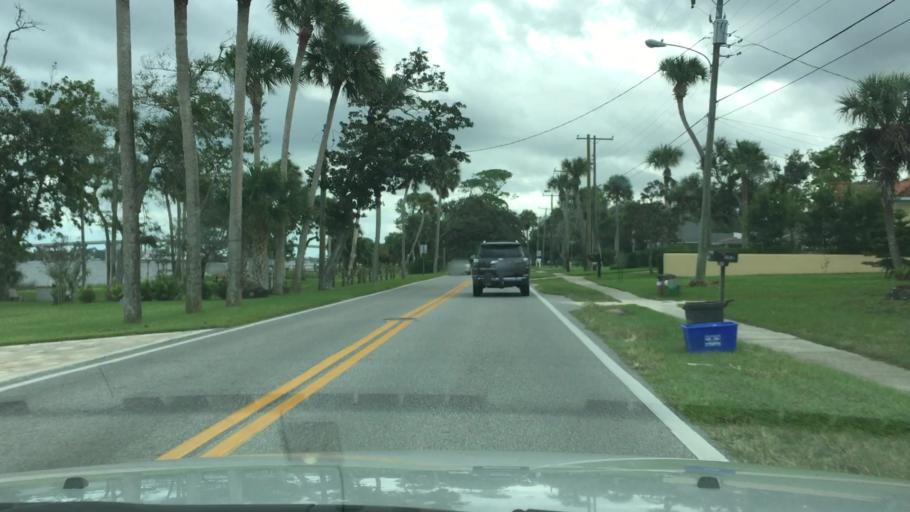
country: US
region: Florida
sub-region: Volusia County
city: Ormond Beach
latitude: 29.2932
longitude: -81.0589
